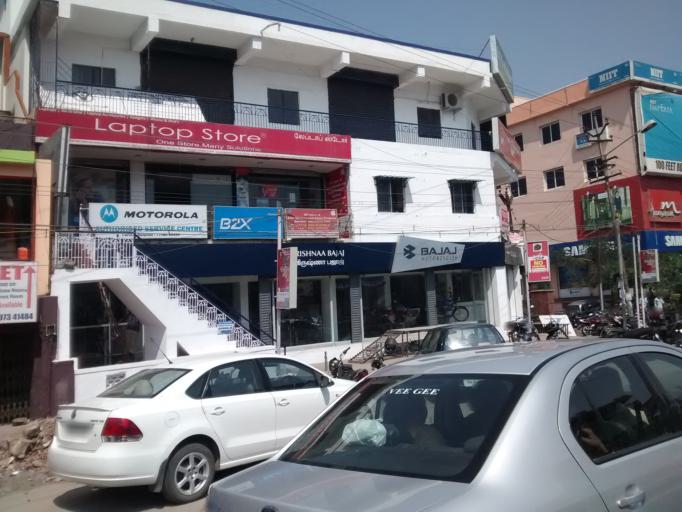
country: IN
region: Tamil Nadu
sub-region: Coimbatore
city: Coimbatore
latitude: 11.0194
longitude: 76.9633
